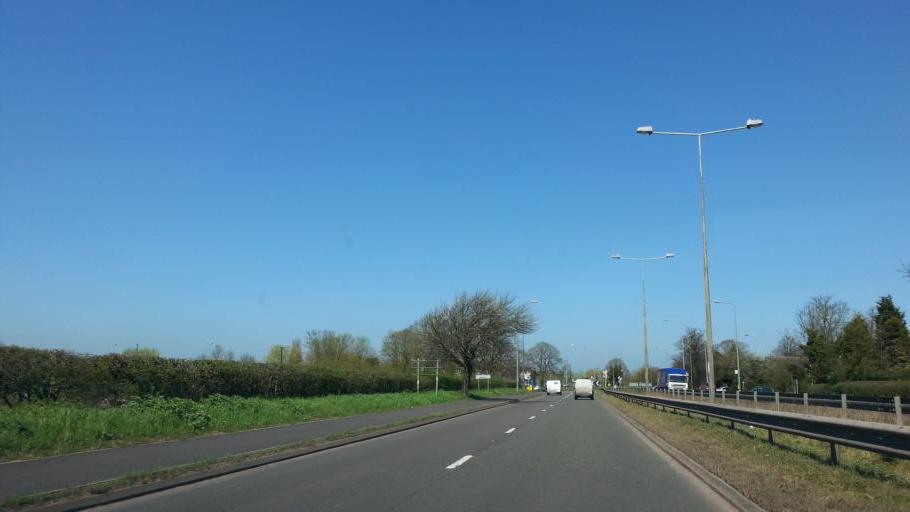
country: GB
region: England
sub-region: Staffordshire
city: Penkridge
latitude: 52.6916
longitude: -2.1316
